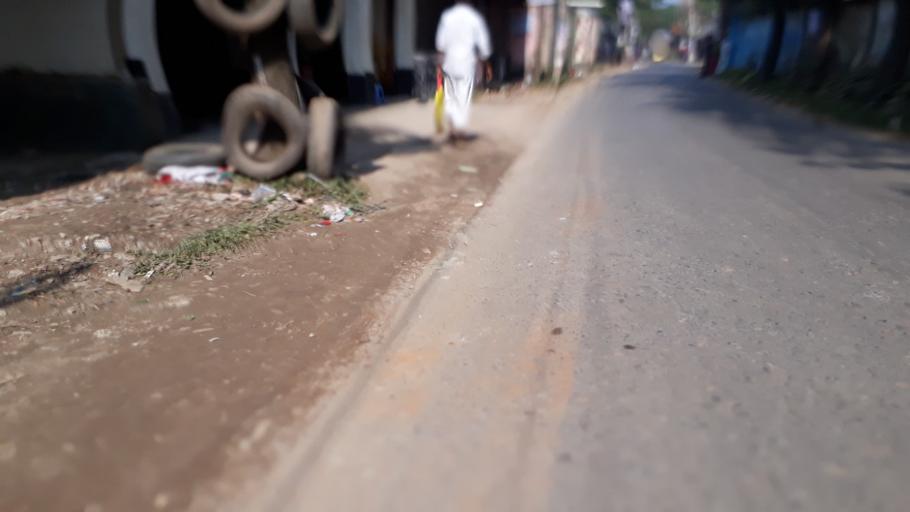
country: BD
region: Dhaka
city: Tungi
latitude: 23.8601
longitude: 90.3108
